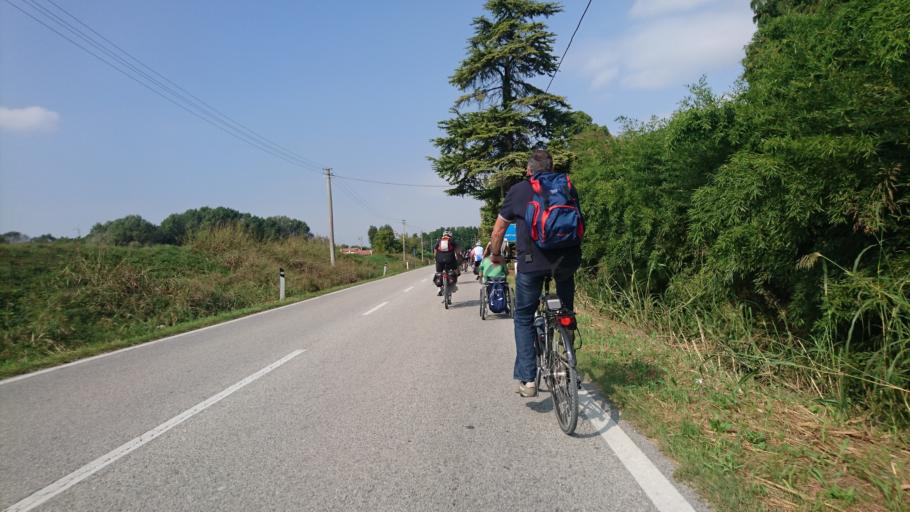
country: IT
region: Veneto
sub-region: Provincia di Padova
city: San Giorgio in Bosco
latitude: 45.5858
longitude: 11.7680
